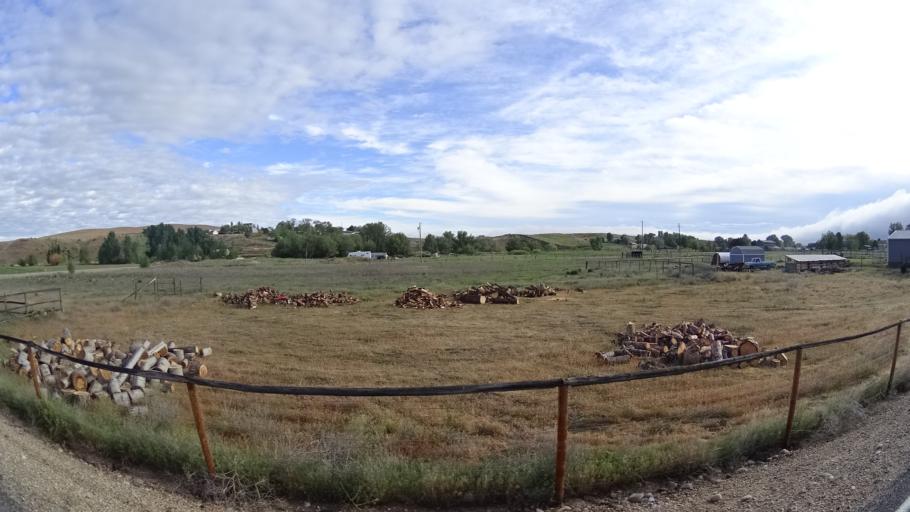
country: US
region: Idaho
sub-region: Ada County
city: Star
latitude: 43.7718
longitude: -116.4894
